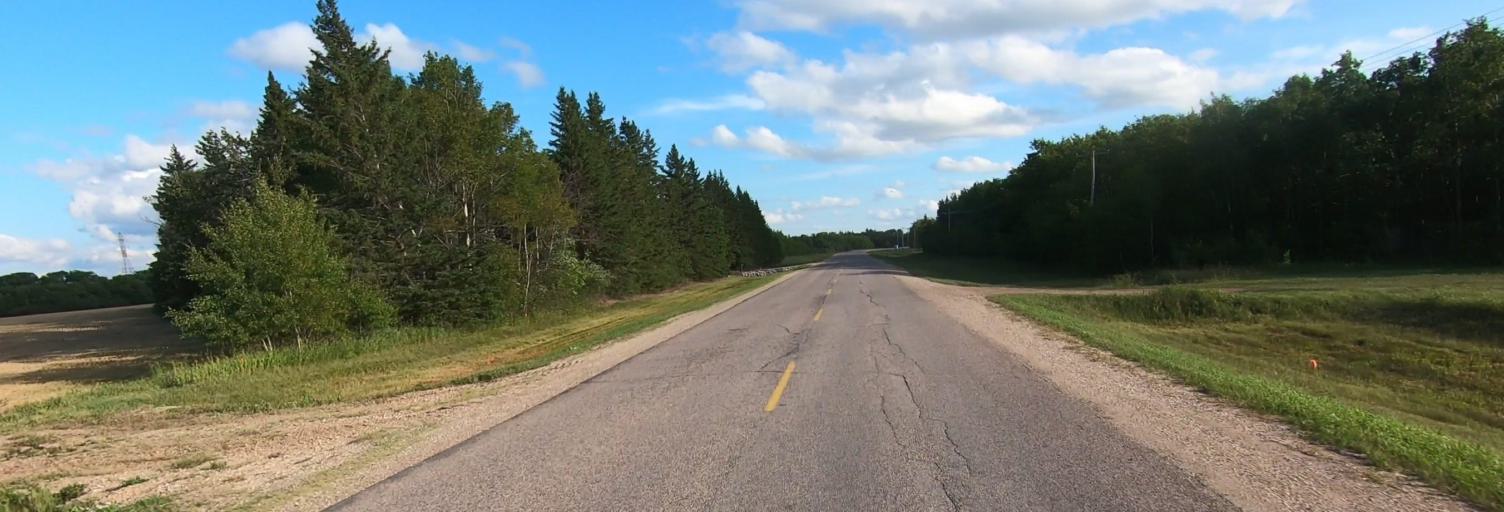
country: CA
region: Manitoba
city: Selkirk
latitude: 50.2066
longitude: -96.8399
